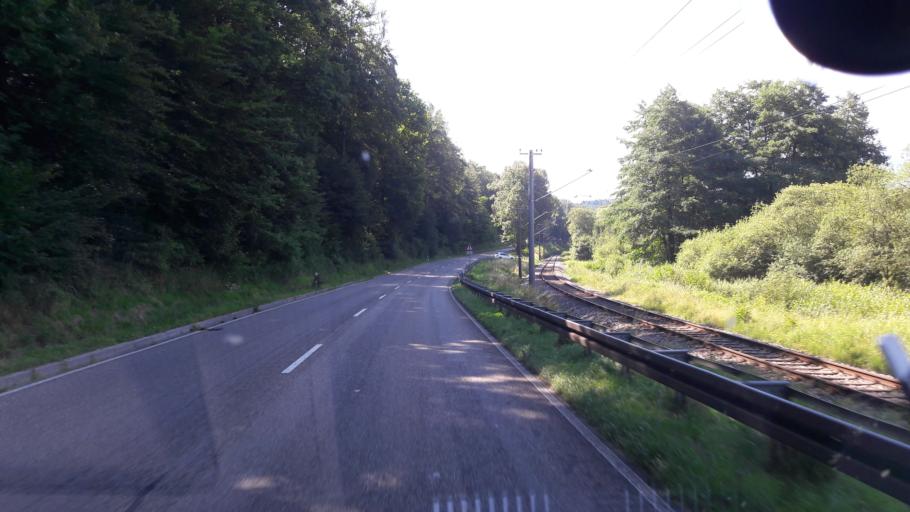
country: DE
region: Baden-Wuerttemberg
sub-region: Karlsruhe Region
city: Ettlingen
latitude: 48.9233
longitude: 8.4557
